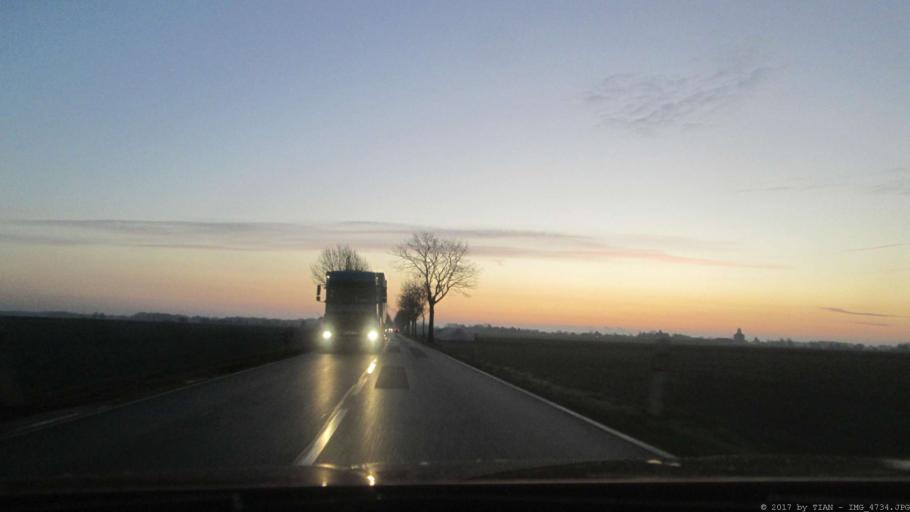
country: DE
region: Lower Saxony
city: Wittingen
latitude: 52.7019
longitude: 10.7892
